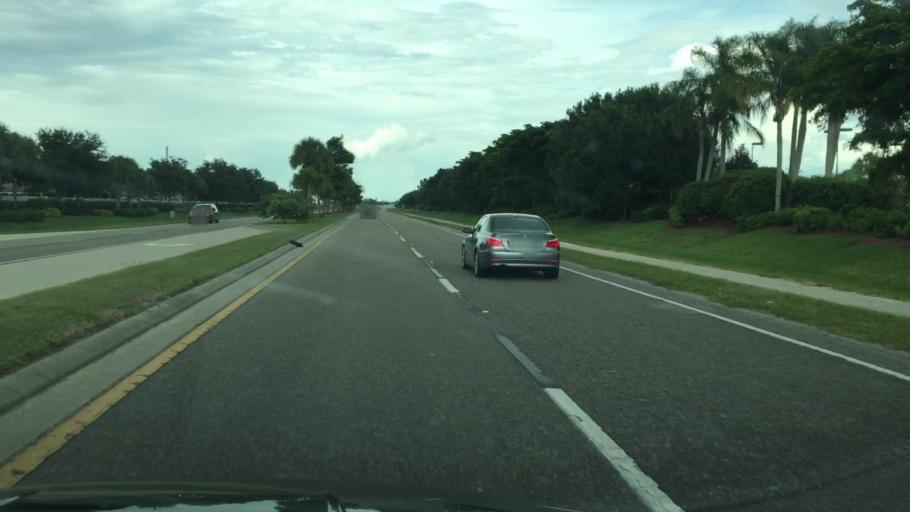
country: US
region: Florida
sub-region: Lee County
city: Estero
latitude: 26.4491
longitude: -81.8004
